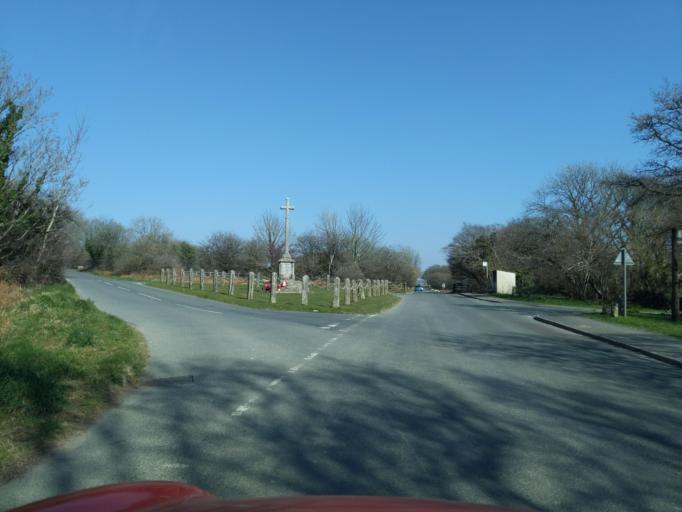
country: GB
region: England
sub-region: Devon
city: Horrabridge
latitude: 50.4909
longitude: -4.1097
